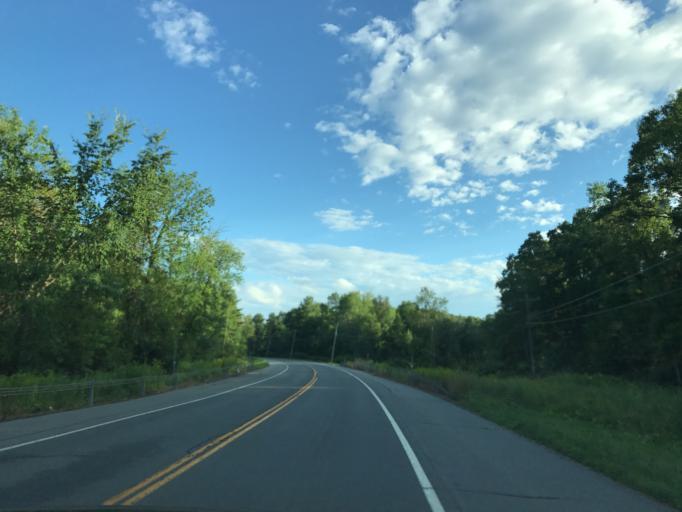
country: US
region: New York
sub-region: Saratoga County
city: Schuylerville
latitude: 43.1417
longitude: -73.5839
